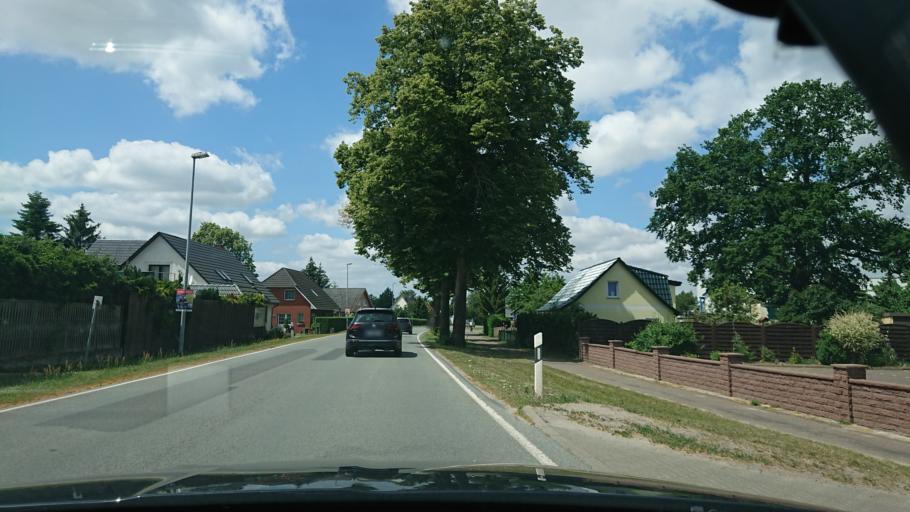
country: DE
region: Brandenburg
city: Perleberg
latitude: 53.0623
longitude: 11.8973
